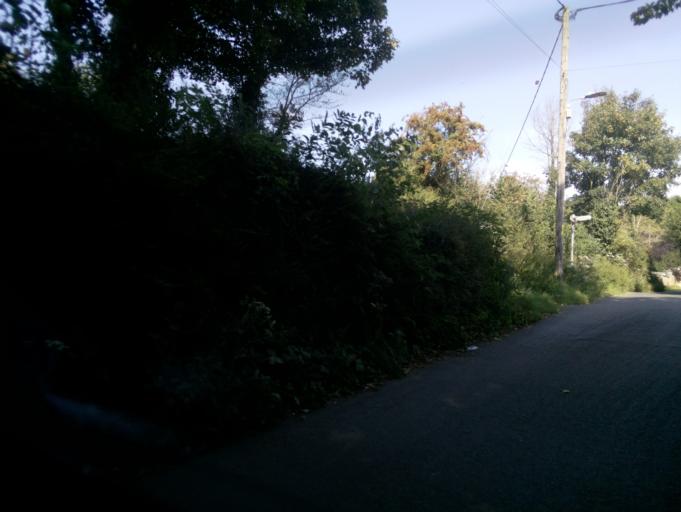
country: GB
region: England
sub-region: Gloucestershire
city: Dursley
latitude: 51.6905
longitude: -2.3430
